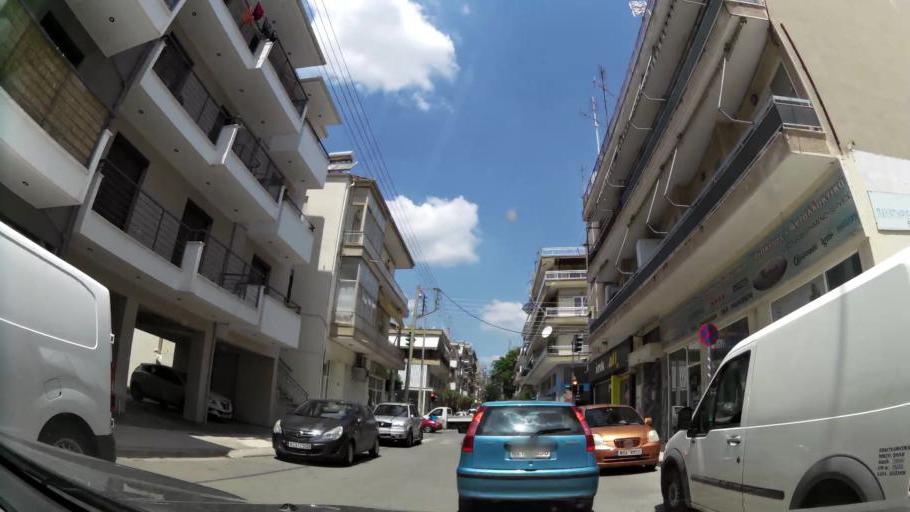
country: GR
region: West Macedonia
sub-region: Nomos Kozanis
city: Kozani
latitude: 40.2970
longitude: 21.7921
